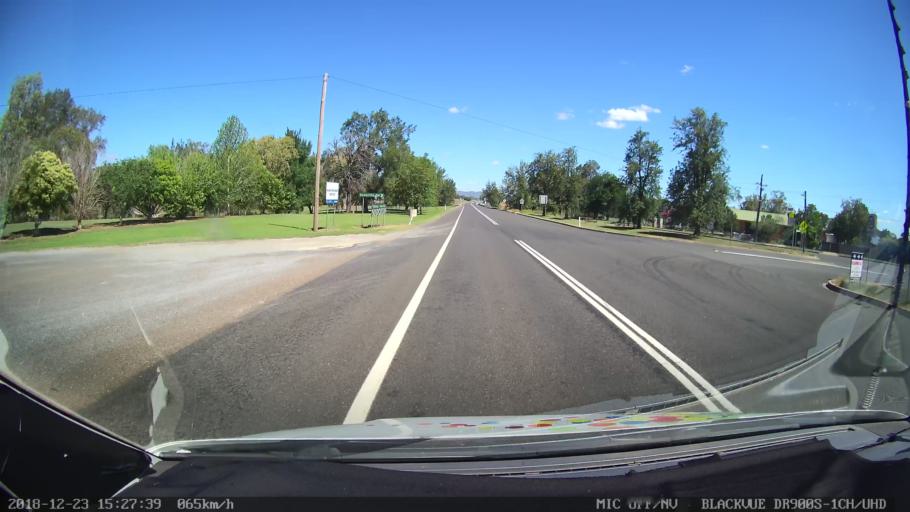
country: AU
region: New South Wales
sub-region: Tamworth Municipality
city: East Tamworth
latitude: -30.9294
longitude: 150.8467
